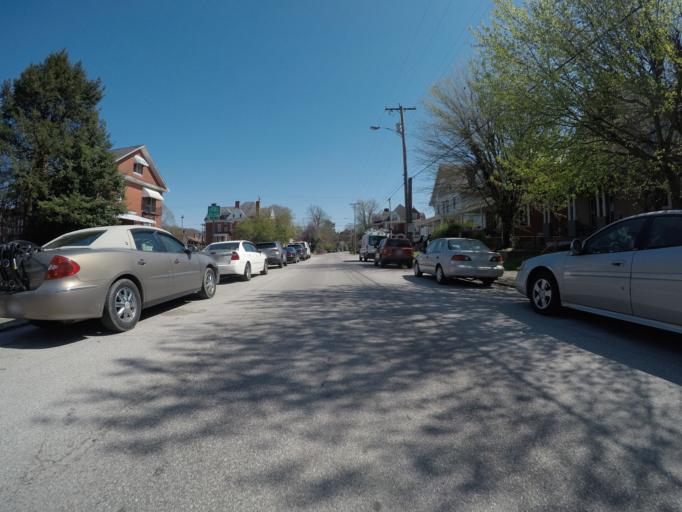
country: US
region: West Virginia
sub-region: Kanawha County
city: Charleston
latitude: 38.3430
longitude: -81.6280
